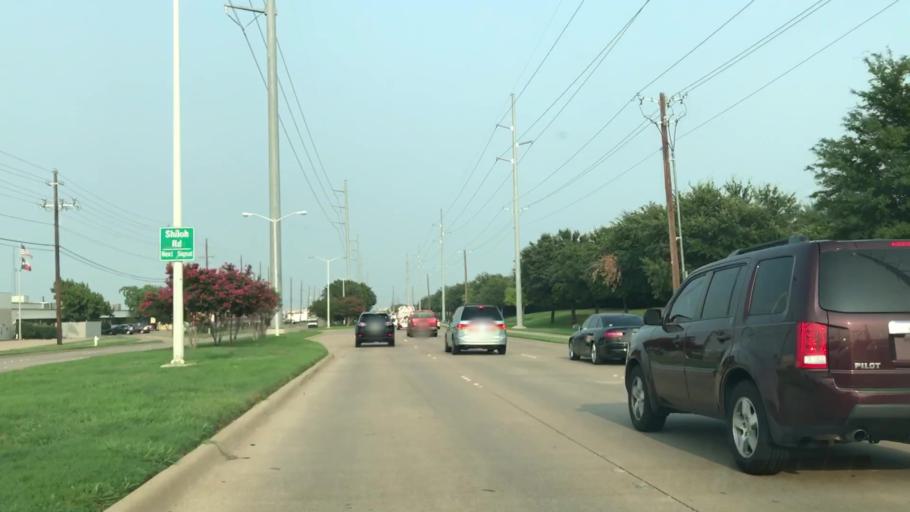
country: US
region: Texas
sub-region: Dallas County
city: Garland
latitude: 32.9091
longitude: -96.6721
